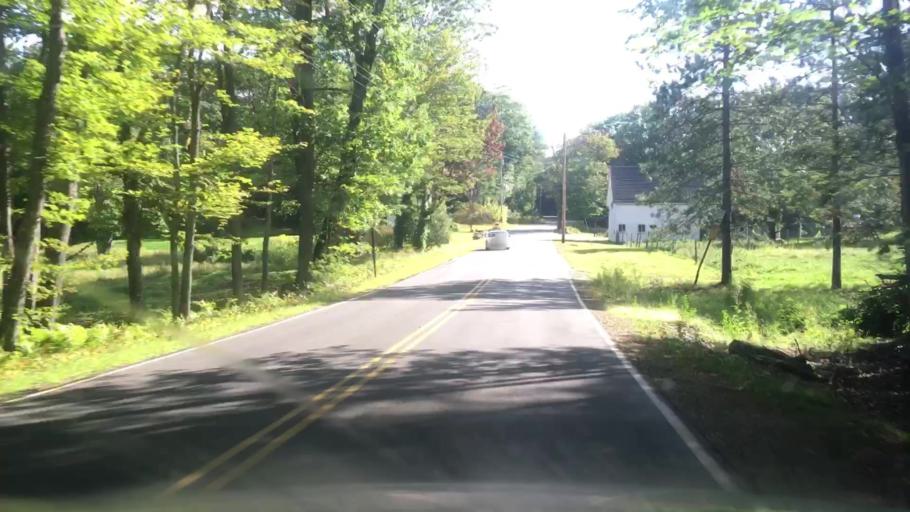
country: US
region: Maine
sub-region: Kennebec County
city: Gardiner
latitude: 44.1641
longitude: -69.7965
